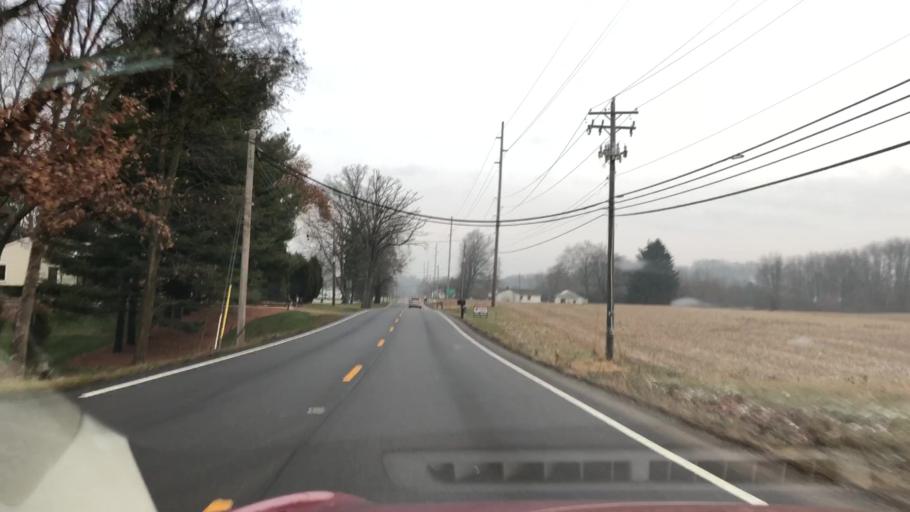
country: US
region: Ohio
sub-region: Stark County
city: Massillon
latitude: 40.8466
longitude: -81.5212
